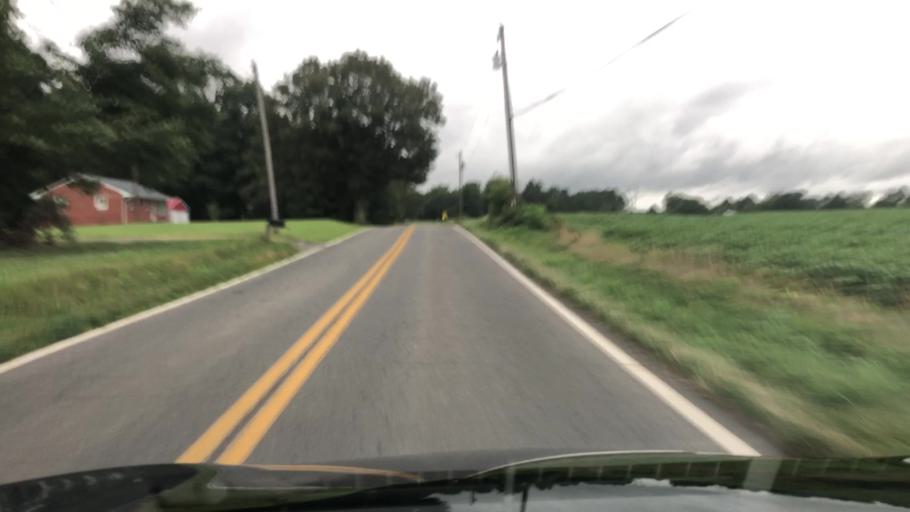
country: US
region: Virginia
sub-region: Prince William County
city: Nokesville
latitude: 38.5865
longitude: -77.6071
